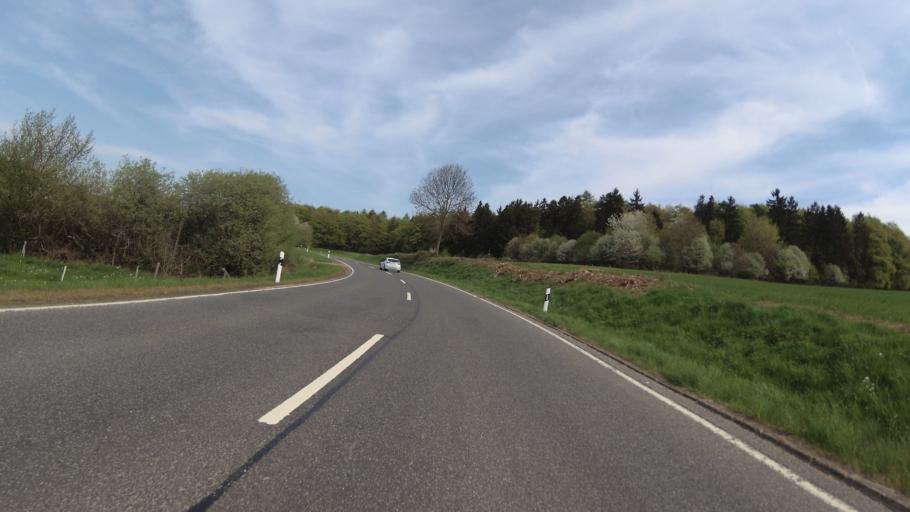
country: DE
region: Rheinland-Pfalz
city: Longkamp
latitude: 49.8675
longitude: 7.1143
